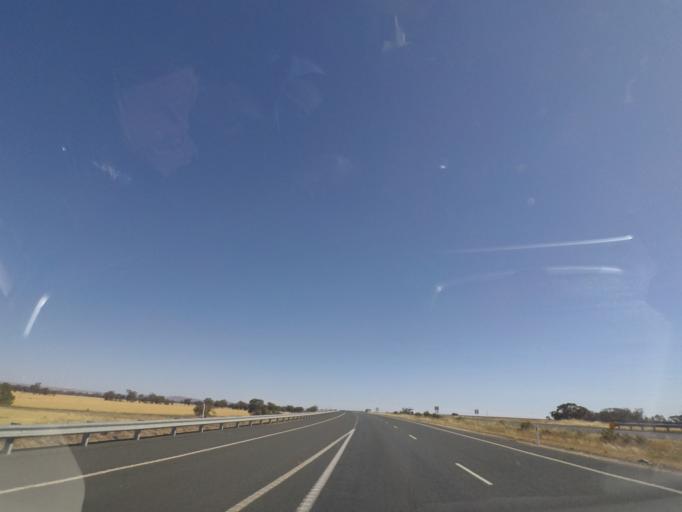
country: AU
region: Victoria
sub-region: Greater Shepparton
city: Shepparton
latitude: -36.7558
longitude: 145.1779
